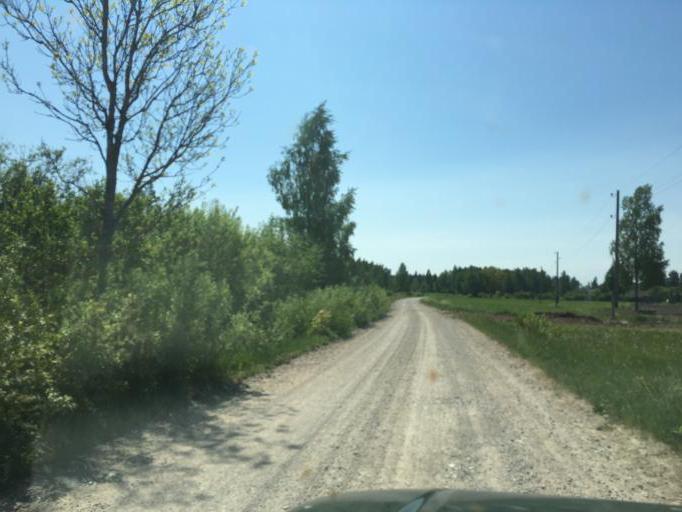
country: LV
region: Rojas
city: Roja
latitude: 57.4305
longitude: 22.7209
